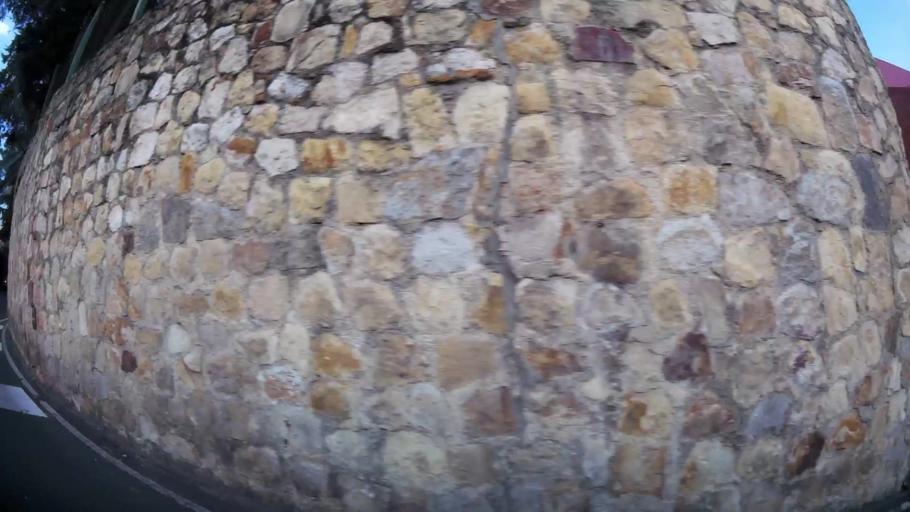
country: CO
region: Bogota D.C.
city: Bogota
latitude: 4.5961
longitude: -74.0688
